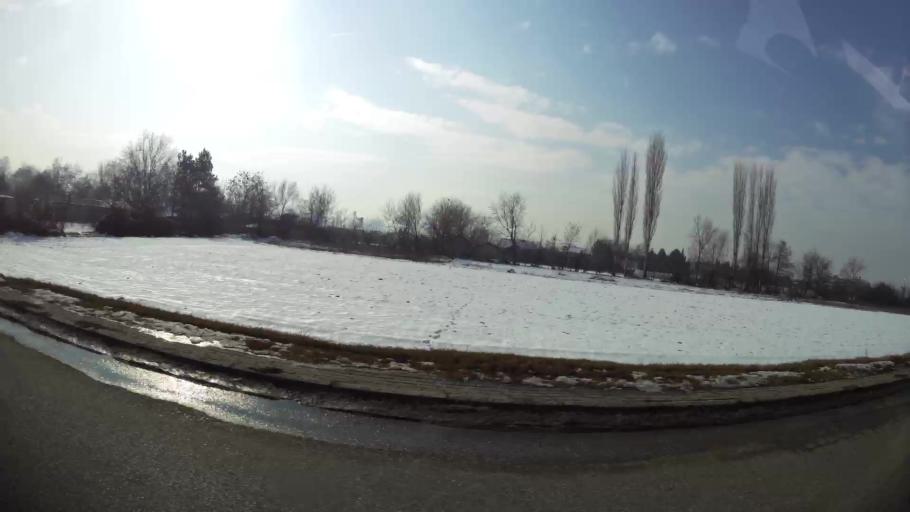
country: MK
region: Suto Orizari
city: Suto Orizare
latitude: 42.0175
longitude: 21.3892
